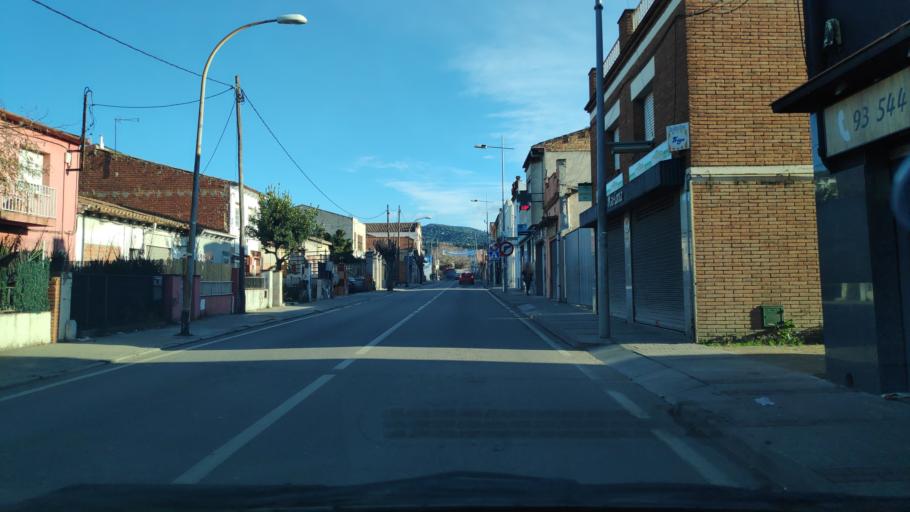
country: ES
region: Catalonia
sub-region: Provincia de Barcelona
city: Mollet del Valles
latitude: 41.5279
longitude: 2.2256
